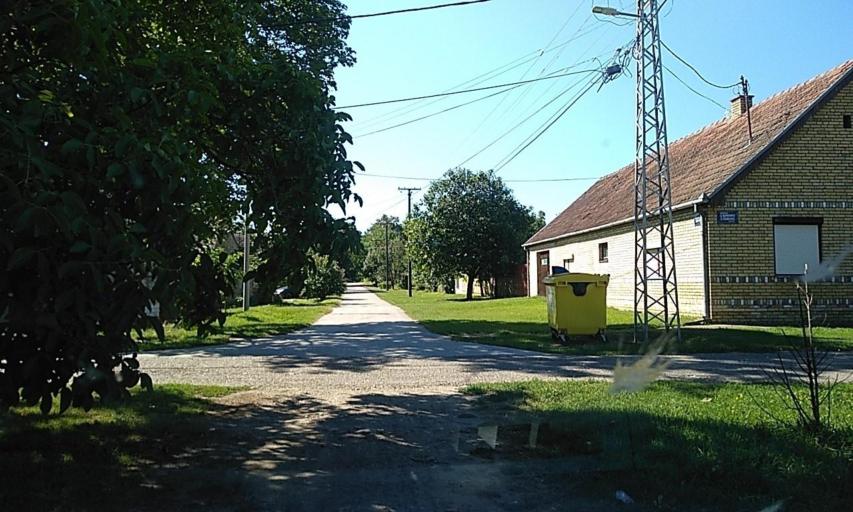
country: RS
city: Backo Gradiste
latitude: 45.5401
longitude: 20.0355
